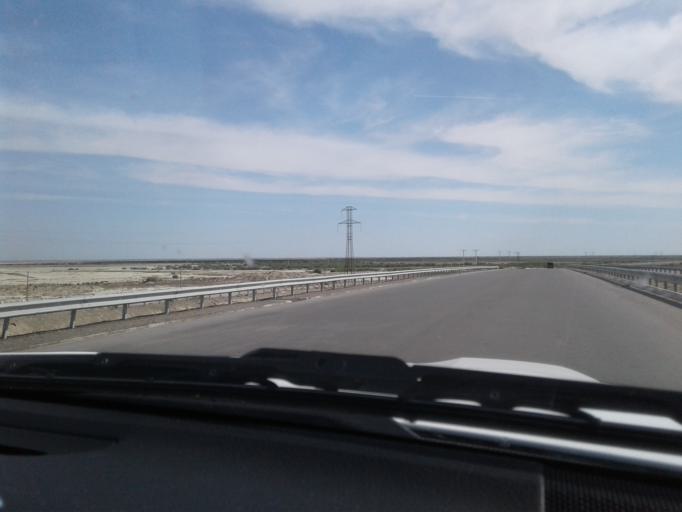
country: TM
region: Balkan
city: Gazanjyk
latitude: 39.2734
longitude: 55.4330
